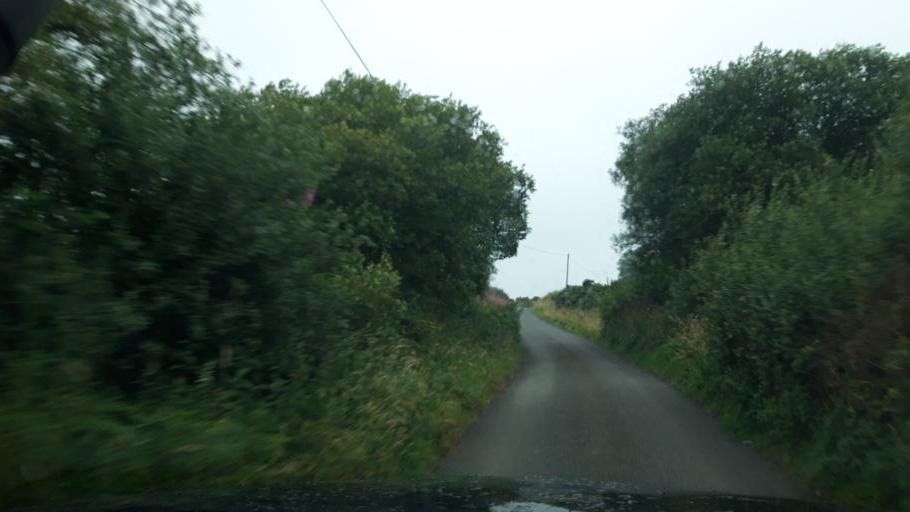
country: IE
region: Leinster
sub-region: Kilkenny
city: Callan
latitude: 52.6367
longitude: -7.5285
